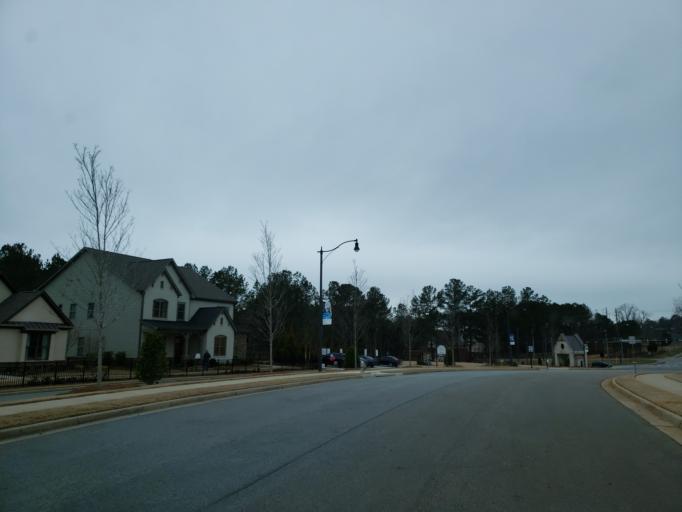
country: US
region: Georgia
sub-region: Cobb County
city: Powder Springs
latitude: 33.9335
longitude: -84.6981
